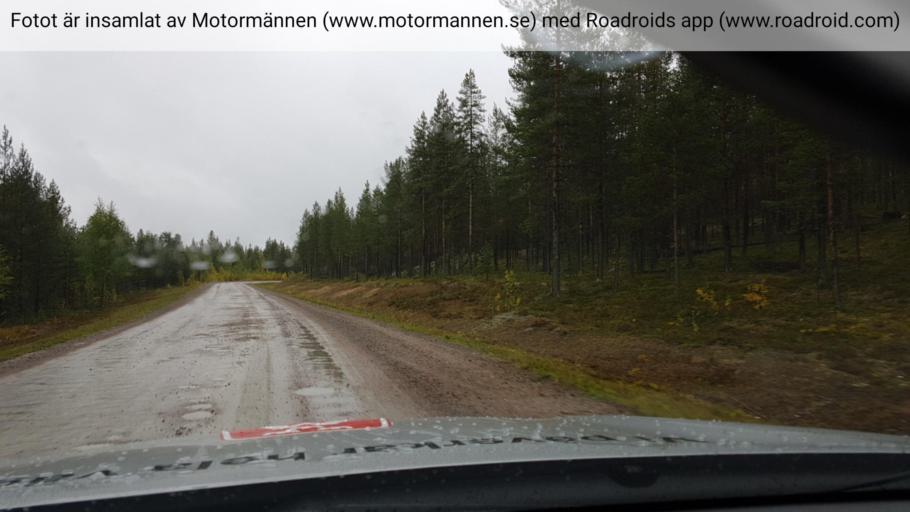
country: SE
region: Norrbotten
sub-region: Alvsbyns Kommun
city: AElvsbyn
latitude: 66.2701
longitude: 21.0889
